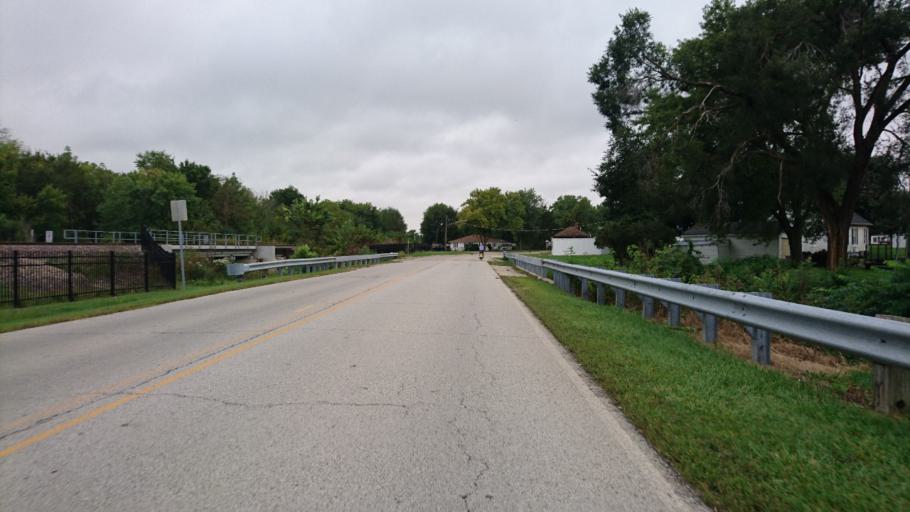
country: US
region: Illinois
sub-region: Livingston County
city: Dwight
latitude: 41.0972
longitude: -88.4225
